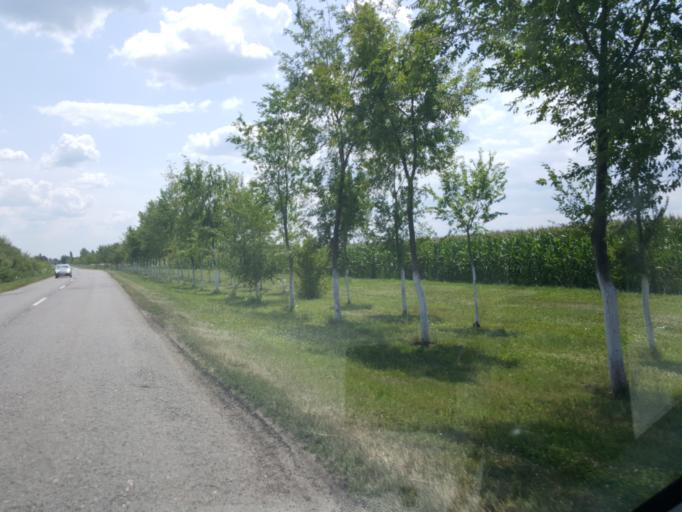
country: RS
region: Autonomna Pokrajina Vojvodina
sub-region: Sremski Okrug
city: Pecinci
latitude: 44.8594
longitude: 19.9601
